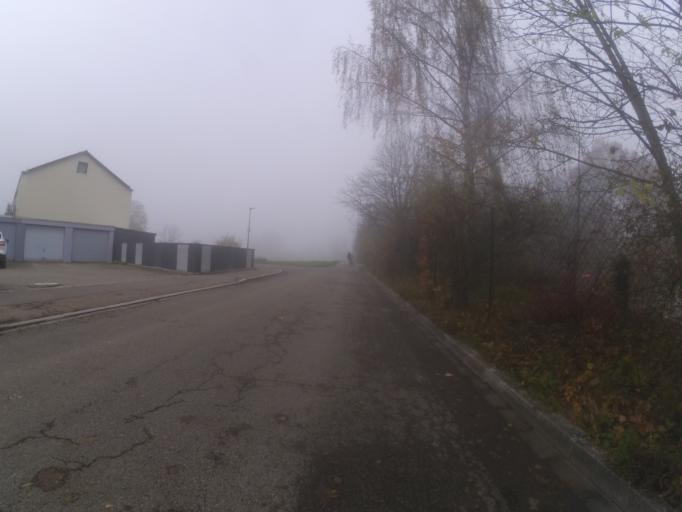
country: DE
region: Bavaria
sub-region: Swabia
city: Neu-Ulm
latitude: 48.3722
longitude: 10.0146
